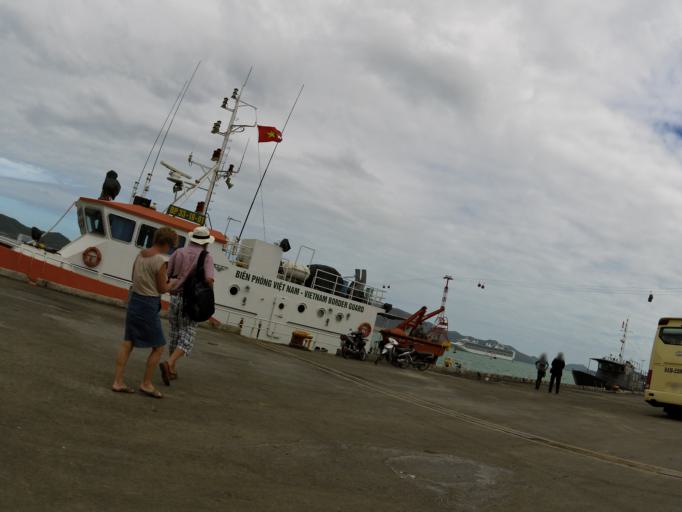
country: VN
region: Khanh Hoa
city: Nha Trang
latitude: 12.2054
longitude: 109.2167
